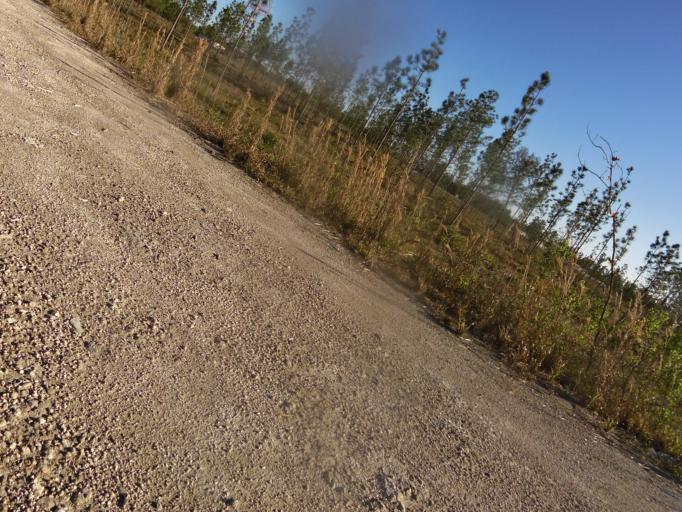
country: US
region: Florida
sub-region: Clay County
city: Keystone Heights
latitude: 29.8368
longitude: -81.9794
